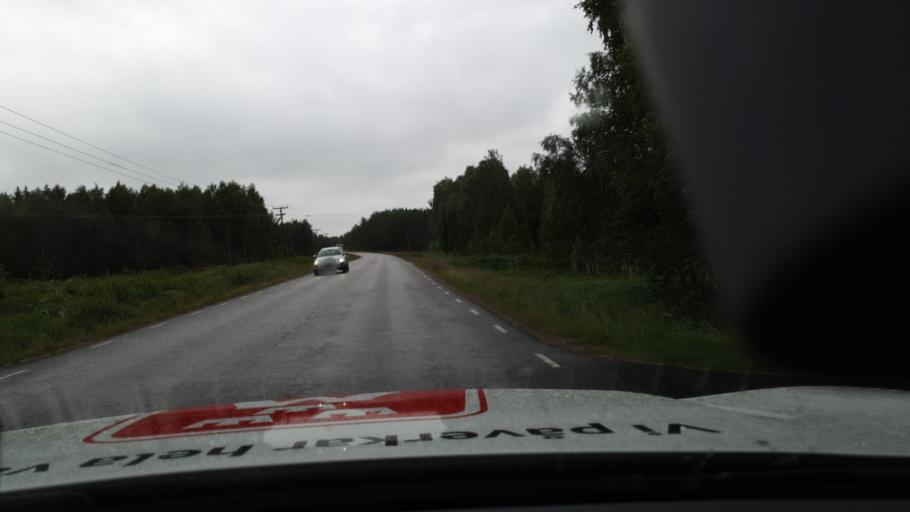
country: SE
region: Norrbotten
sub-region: Overtornea Kommun
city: OEvertornea
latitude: 66.4673
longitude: 23.6590
